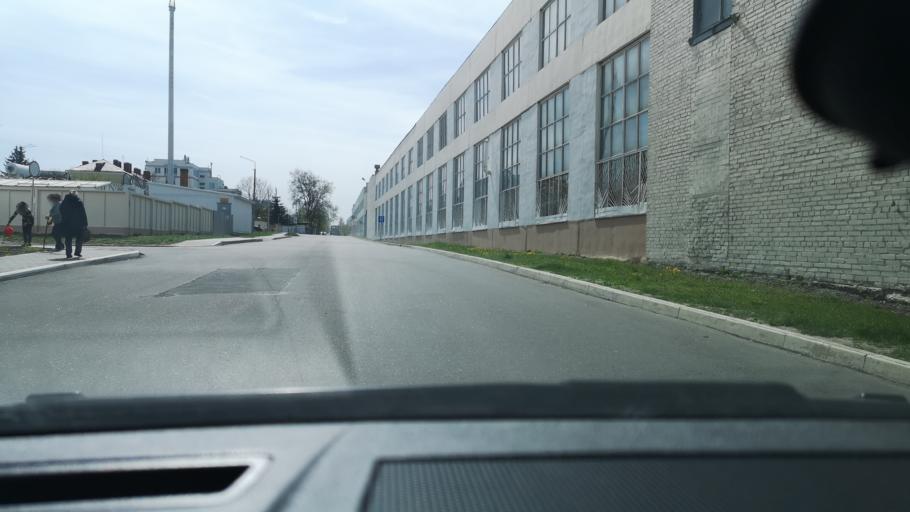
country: BY
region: Gomel
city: Gomel
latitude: 52.4223
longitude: 31.0105
